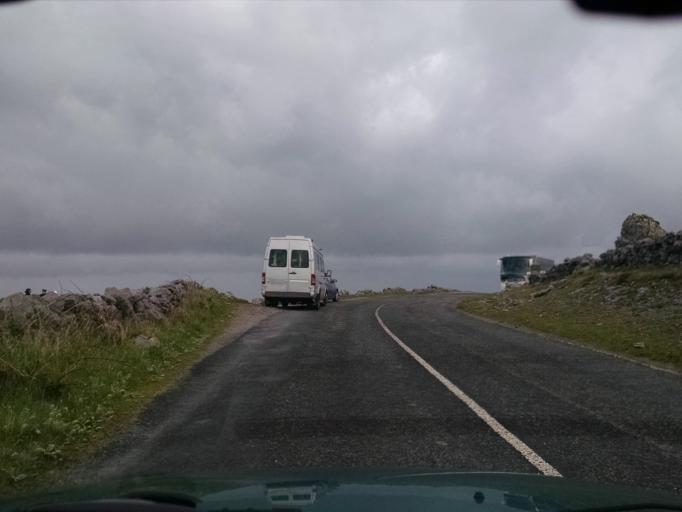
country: IE
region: Connaught
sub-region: County Galway
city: Bearna
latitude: 53.0602
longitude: -9.3621
